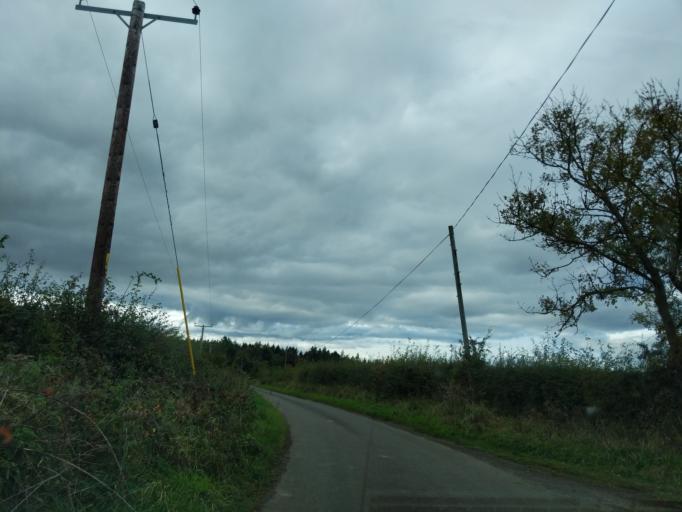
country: GB
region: Scotland
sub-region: East Lothian
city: Macmerry
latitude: 55.9437
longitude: -2.8614
